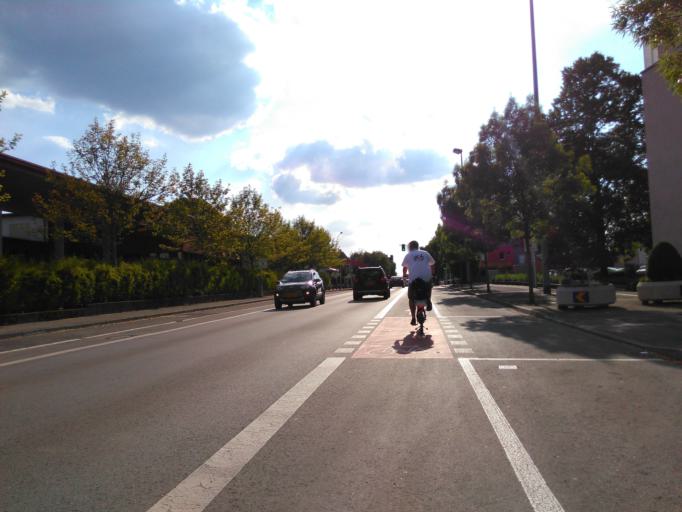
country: LU
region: Luxembourg
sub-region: Canton d'Esch-sur-Alzette
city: Esch-sur-Alzette
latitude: 49.5105
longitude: 5.9892
